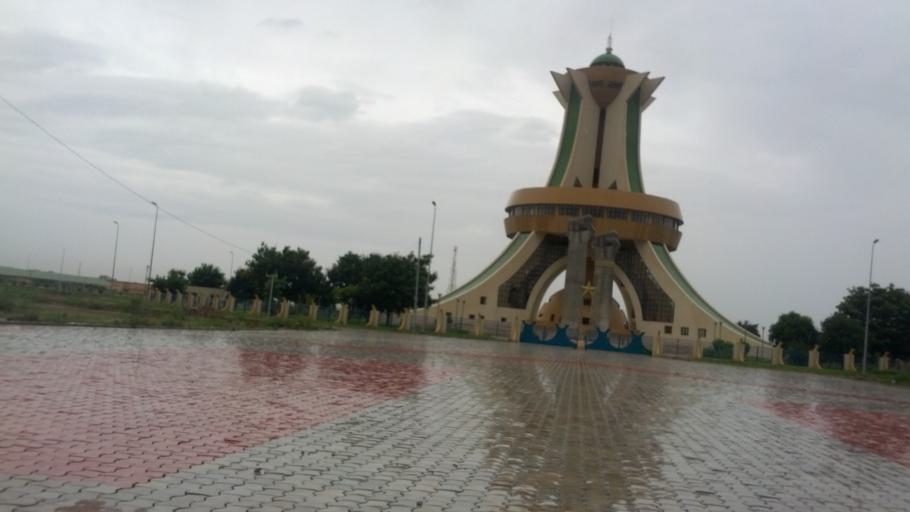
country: BF
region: Centre
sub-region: Kadiogo Province
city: Ouagadougou
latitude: 12.3108
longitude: -1.5027
